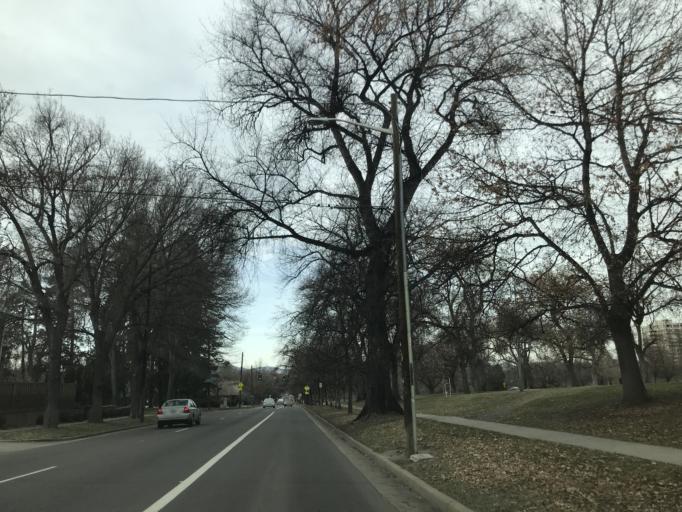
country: US
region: Colorado
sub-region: Denver County
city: Denver
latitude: 39.7292
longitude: -104.9640
